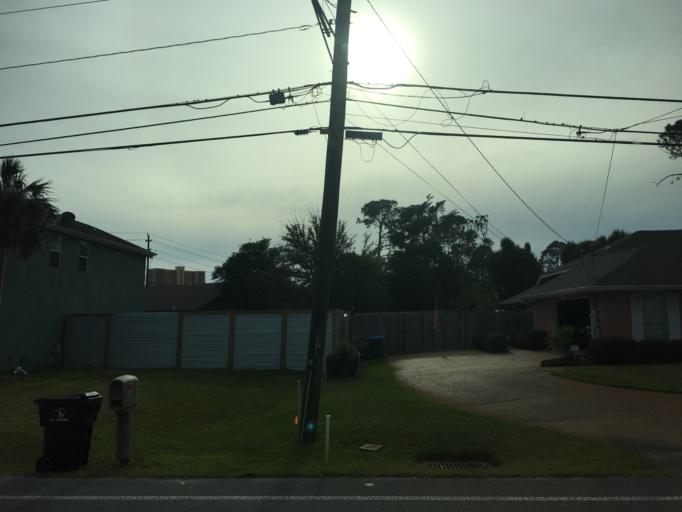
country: US
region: Florida
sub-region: Bay County
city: Panama City Beach
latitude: 30.1691
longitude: -85.7824
